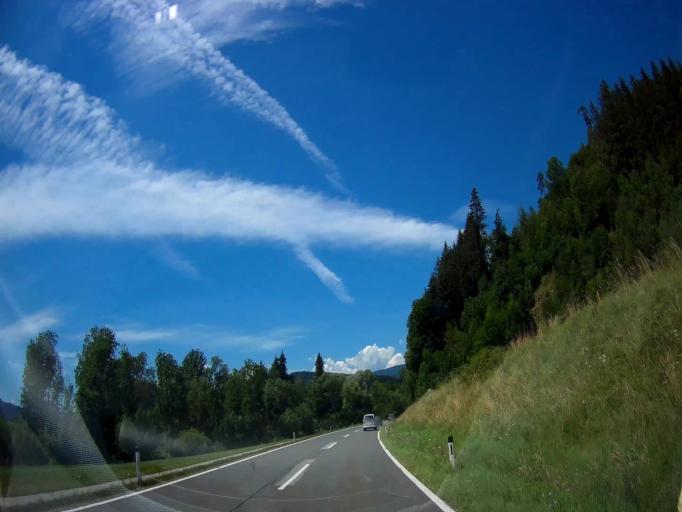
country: AT
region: Carinthia
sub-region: Politischer Bezirk Sankt Veit an der Glan
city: Micheldorf
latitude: 46.9017
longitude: 14.3748
